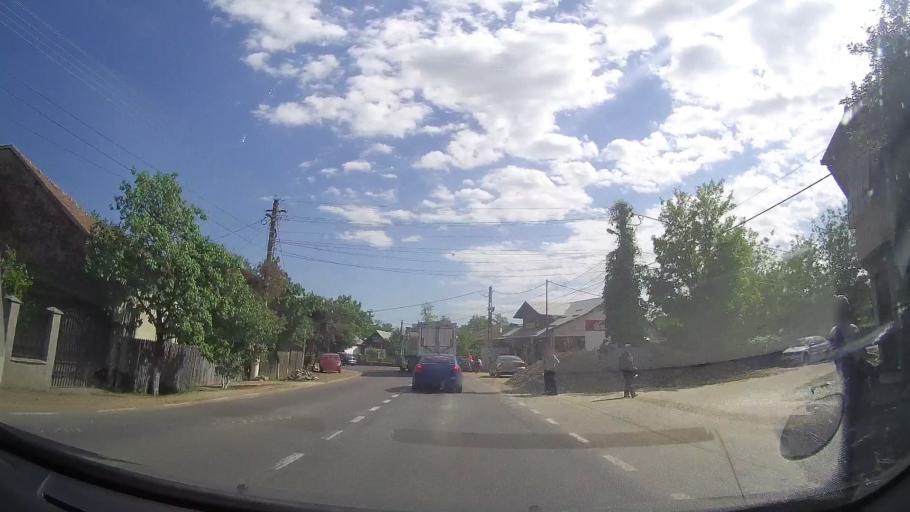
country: RO
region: Prahova
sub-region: Comuna Izvoarele
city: Homoraciu
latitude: 45.2787
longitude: 26.0094
